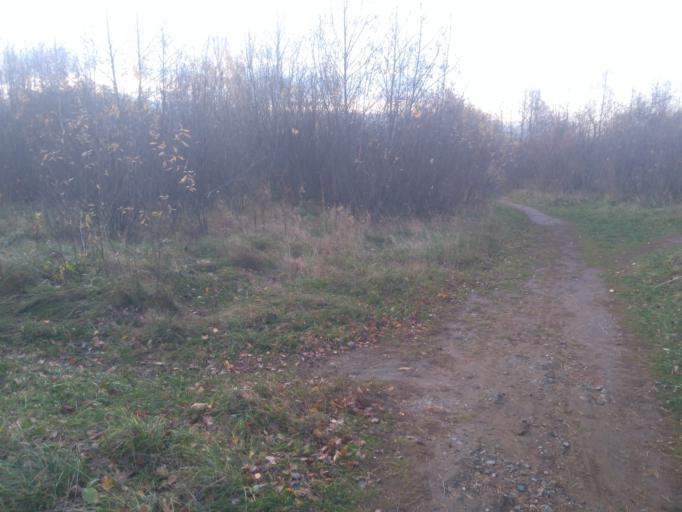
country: RU
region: Tatarstan
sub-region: Tukayevskiy Rayon
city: Naberezhnyye Chelny
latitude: 55.7658
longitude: 52.4000
